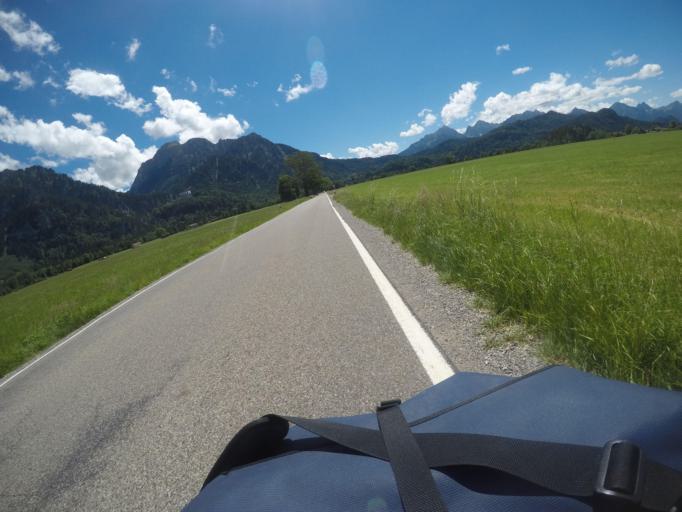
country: DE
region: Bavaria
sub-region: Swabia
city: Schwangau
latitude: 47.5716
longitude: 10.7455
